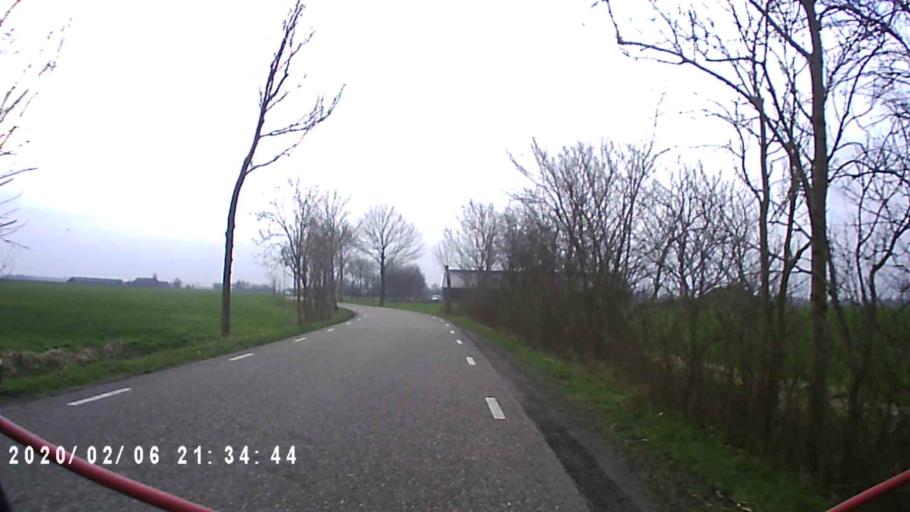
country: NL
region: Groningen
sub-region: Gemeente Zuidhorn
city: Noordhorn
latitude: 53.2725
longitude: 6.3903
